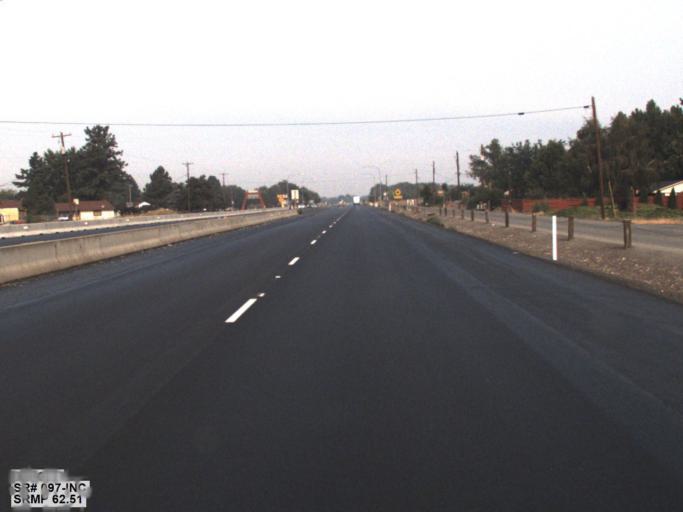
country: US
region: Washington
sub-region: Yakima County
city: Toppenish
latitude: 46.3792
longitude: -120.3375
